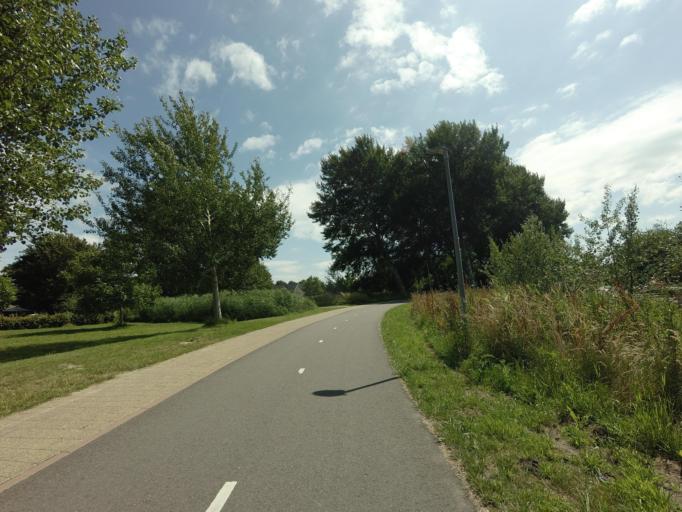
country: NL
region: Flevoland
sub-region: Gemeente Almere
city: Almere Stad
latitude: 52.3455
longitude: 5.2061
